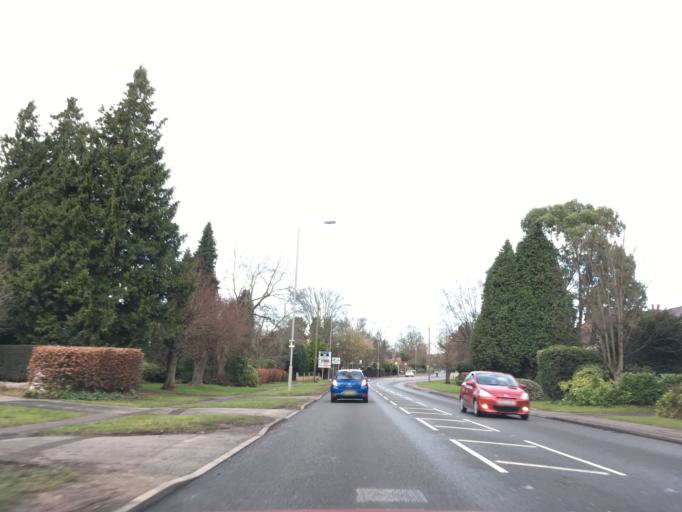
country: GB
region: England
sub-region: Nottinghamshire
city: Ruddington
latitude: 52.8901
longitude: -1.1425
